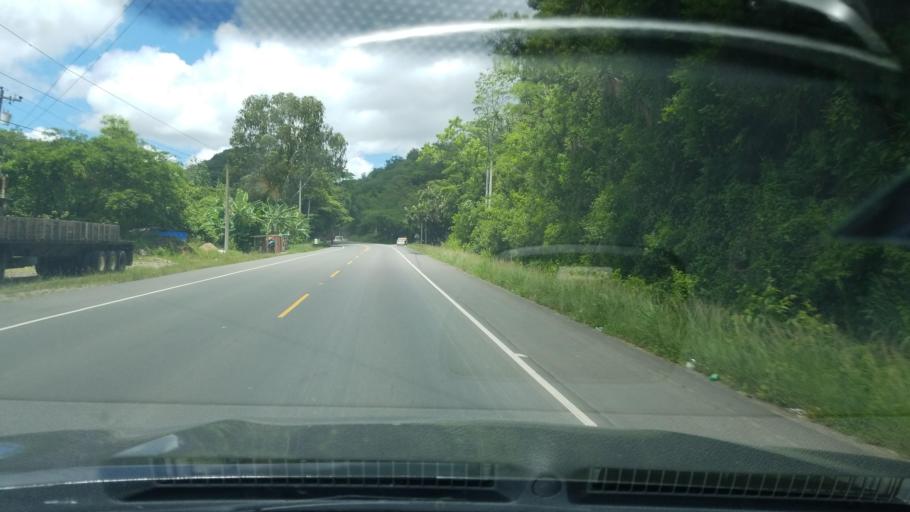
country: HN
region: Francisco Morazan
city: Talanga
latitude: 14.3799
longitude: -87.1366
